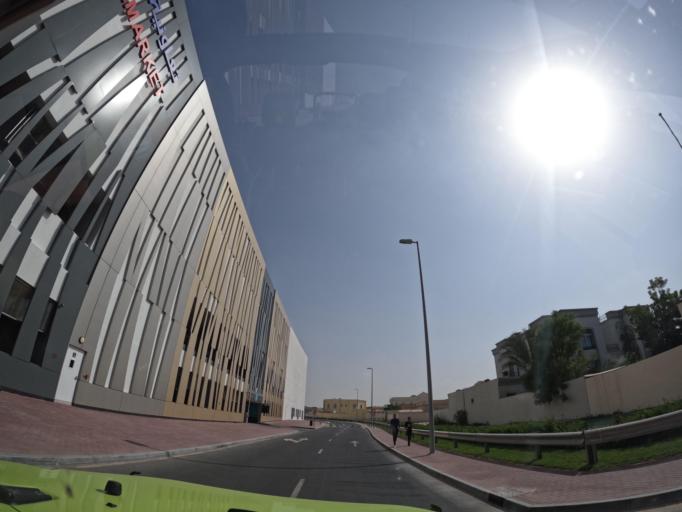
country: AE
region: Ash Shariqah
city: Sharjah
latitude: 25.2060
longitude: 55.4255
